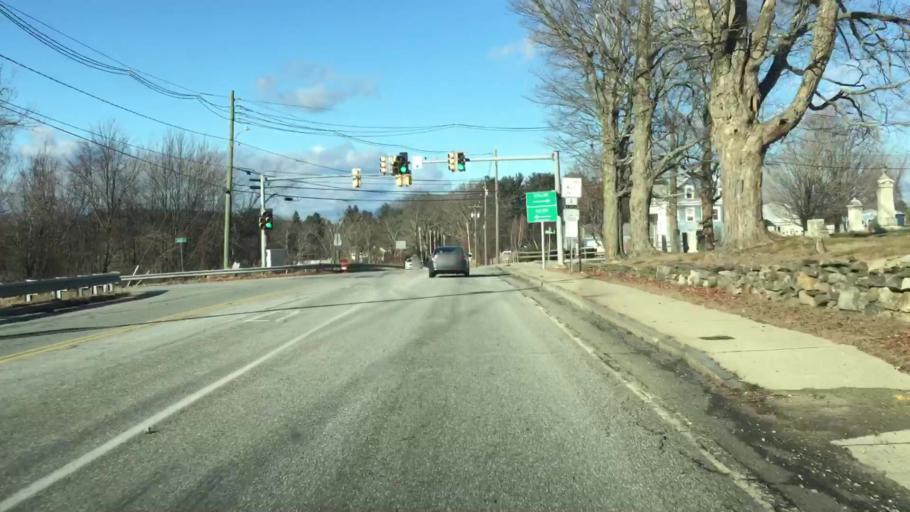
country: US
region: Massachusetts
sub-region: Worcester County
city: West Boylston
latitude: 42.4067
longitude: -71.7989
